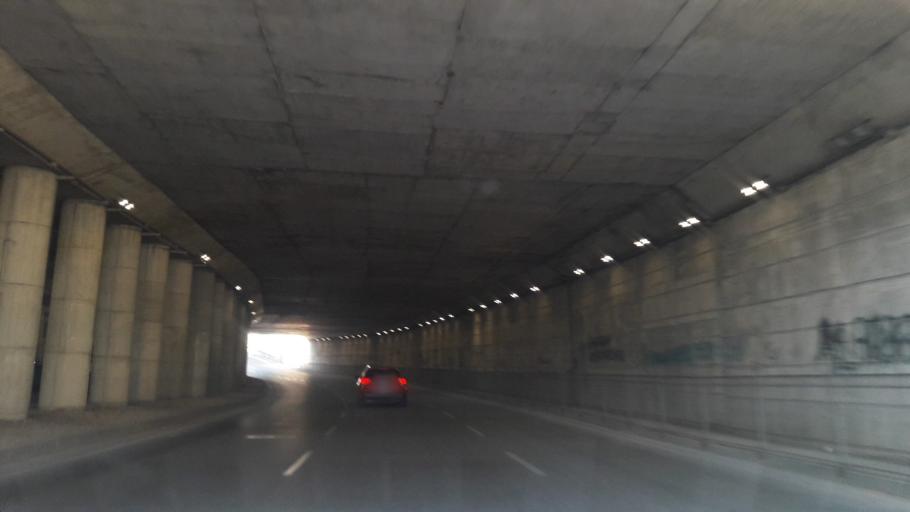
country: TR
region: Adana
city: Seyhan
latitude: 36.9968
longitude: 35.3015
